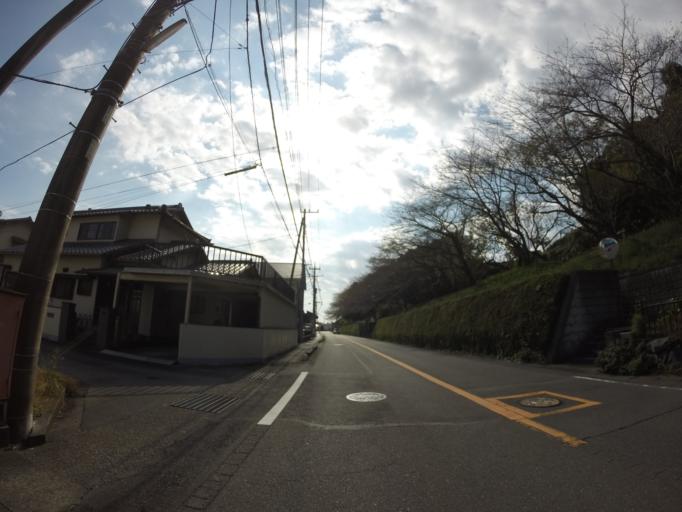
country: JP
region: Shizuoka
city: Fujinomiya
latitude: 35.1777
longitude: 138.6373
